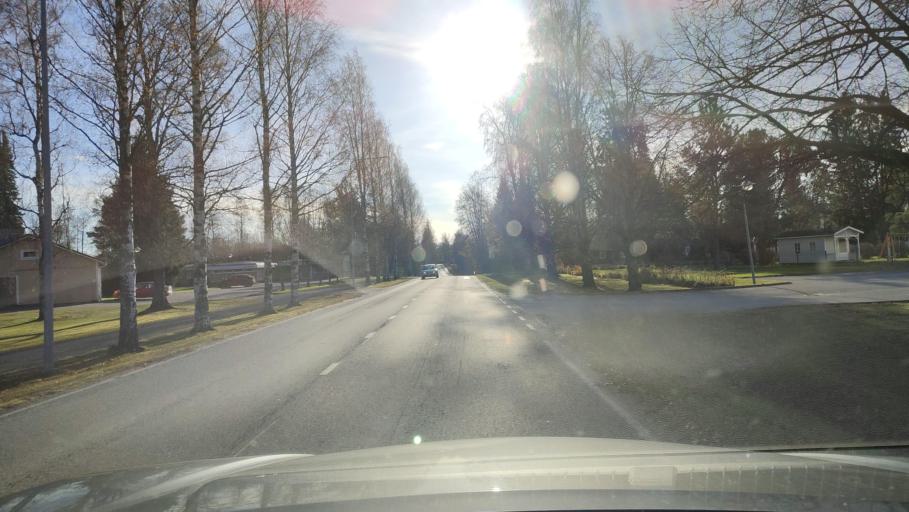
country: FI
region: Southern Ostrobothnia
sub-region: Suupohja
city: Teuva
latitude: 62.4790
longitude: 21.7394
